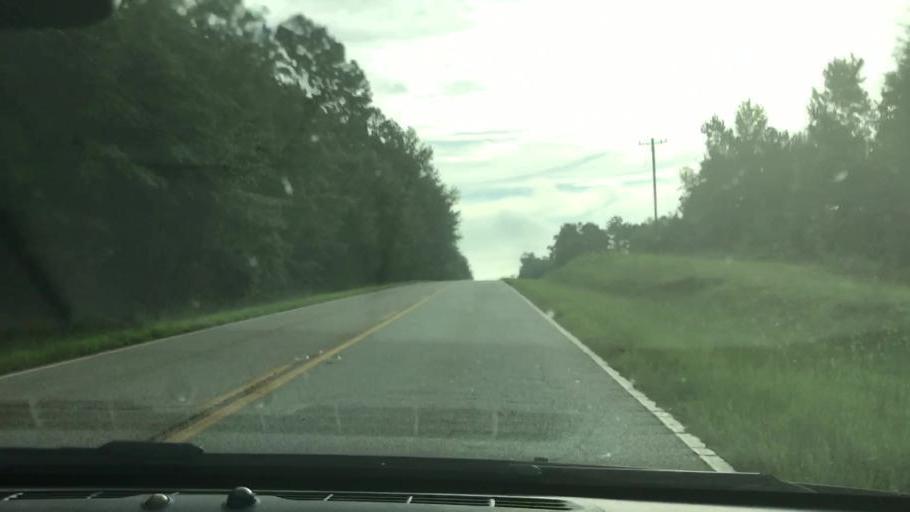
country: US
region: Georgia
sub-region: Quitman County
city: Georgetown
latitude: 31.8942
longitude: -85.0670
